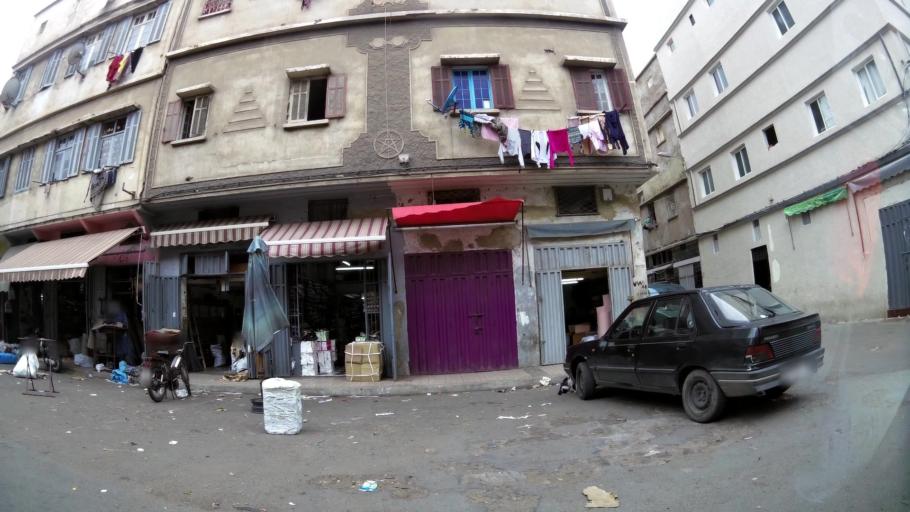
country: MA
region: Grand Casablanca
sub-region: Casablanca
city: Casablanca
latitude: 33.5694
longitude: -7.6053
